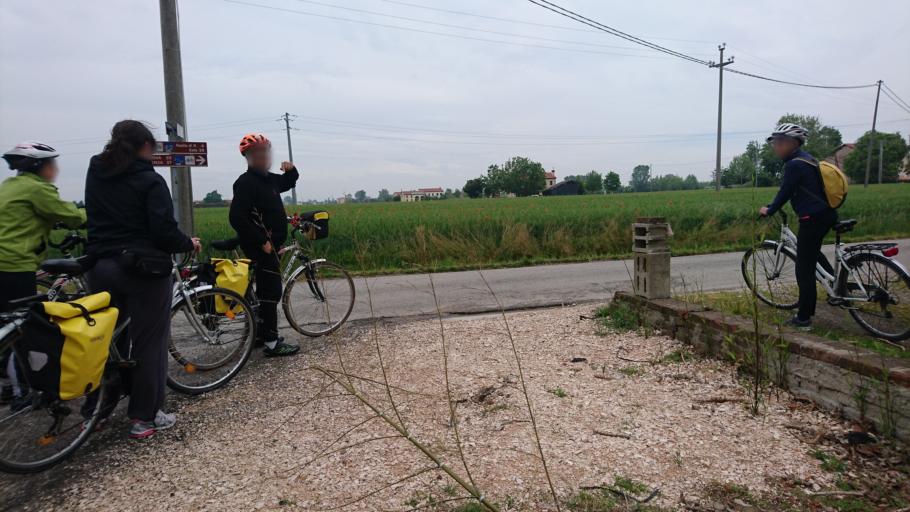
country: IT
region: Veneto
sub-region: Provincia di Padova
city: Montemerlo
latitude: 45.3903
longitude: 11.6904
